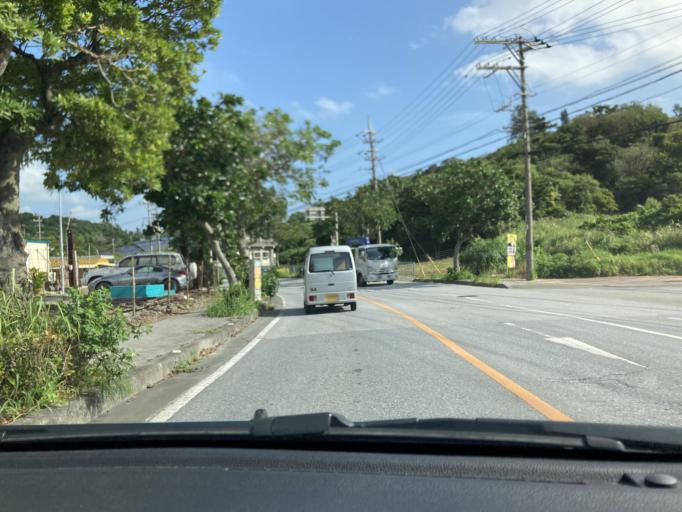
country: JP
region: Okinawa
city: Ginowan
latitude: 26.2728
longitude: 127.7810
